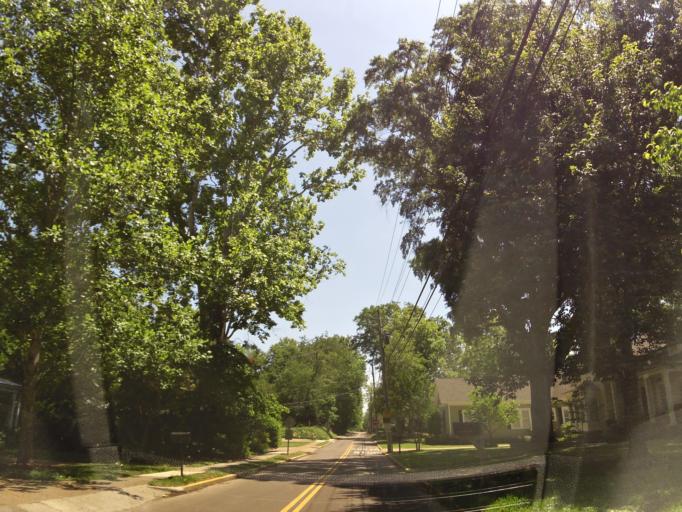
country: US
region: Mississippi
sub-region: Lafayette County
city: Oxford
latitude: 34.3706
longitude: -89.5163
